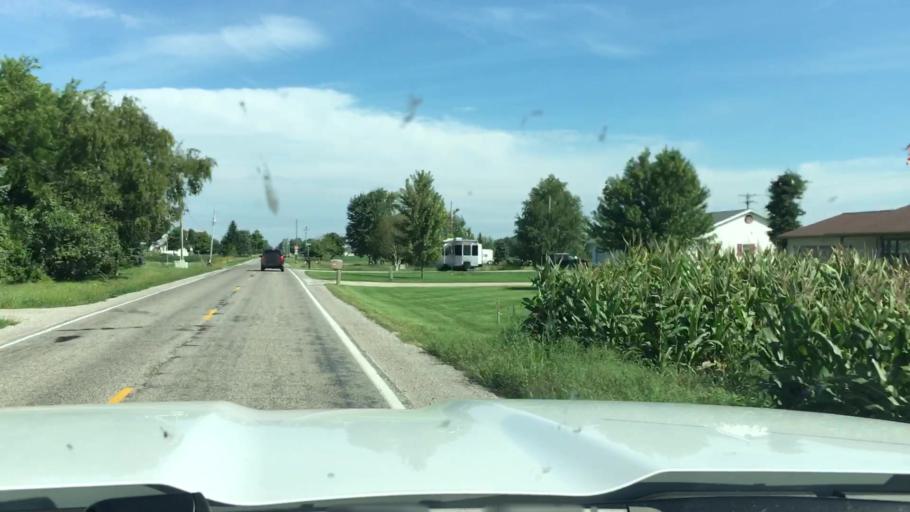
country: US
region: Michigan
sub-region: Saginaw County
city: Hemlock
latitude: 43.4281
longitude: -84.2299
